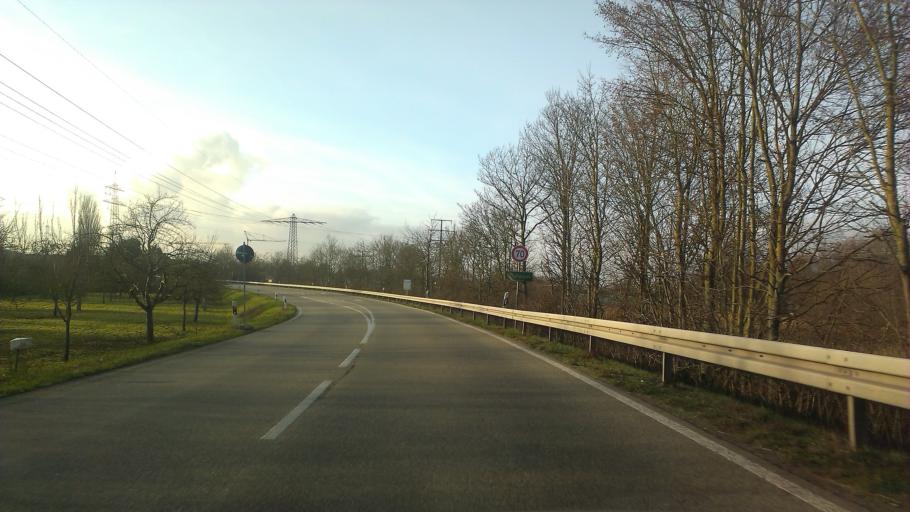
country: DE
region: Baden-Wuerttemberg
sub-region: Karlsruhe Region
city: Waghausel
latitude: 49.2556
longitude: 8.5119
